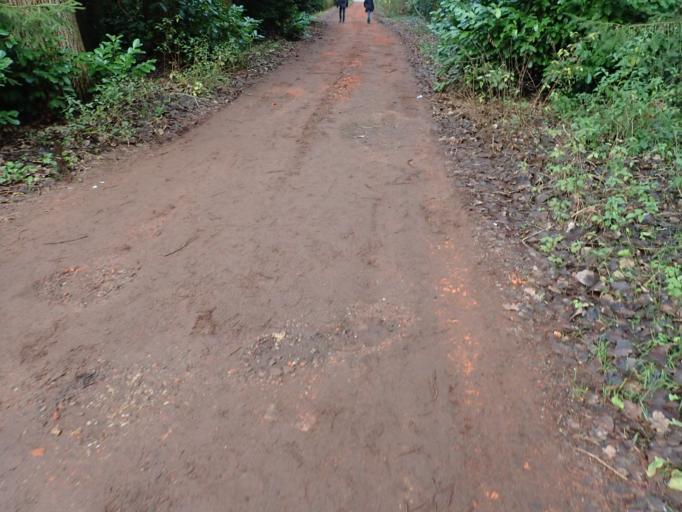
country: BE
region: Flanders
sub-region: Provincie Antwerpen
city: Zandhoven
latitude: 51.2254
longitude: 4.6280
